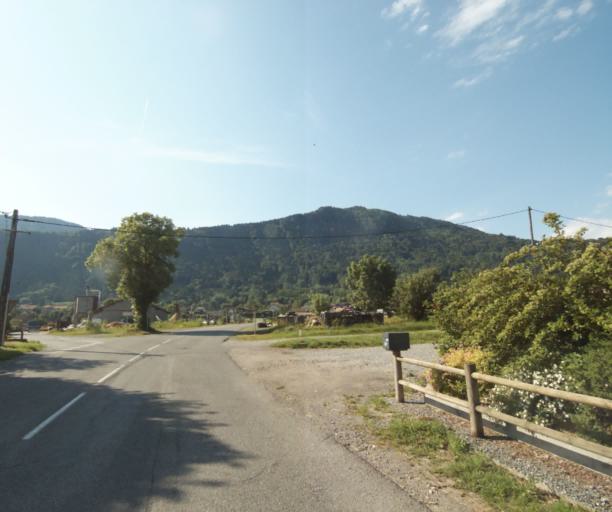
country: FR
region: Rhone-Alpes
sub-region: Departement de la Haute-Savoie
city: Allinges
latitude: 46.3148
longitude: 6.4845
